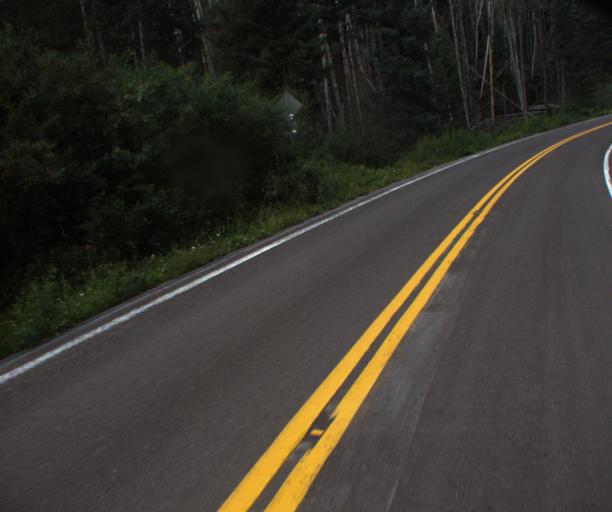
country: US
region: Arizona
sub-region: Greenlee County
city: Morenci
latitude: 33.5689
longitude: -109.3575
